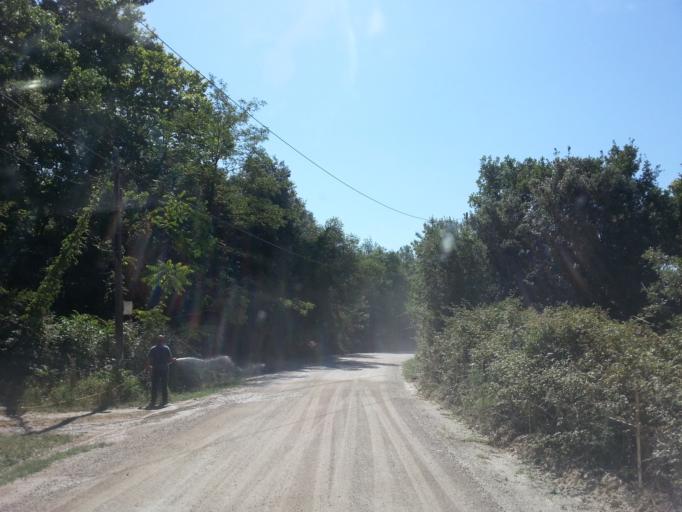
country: ES
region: Catalonia
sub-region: Provincia de Barcelona
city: Campins
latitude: 41.7388
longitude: 2.4987
